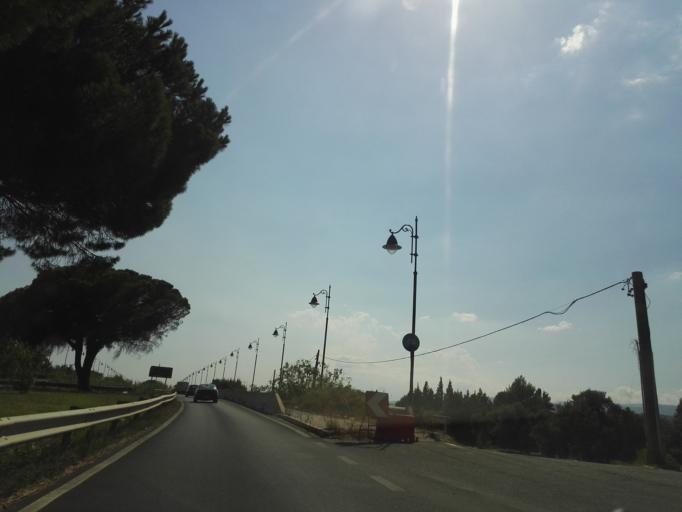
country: IT
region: Calabria
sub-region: Provincia di Reggio Calabria
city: Marina di Gioiosa Ionica
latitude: 38.2983
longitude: 16.3257
